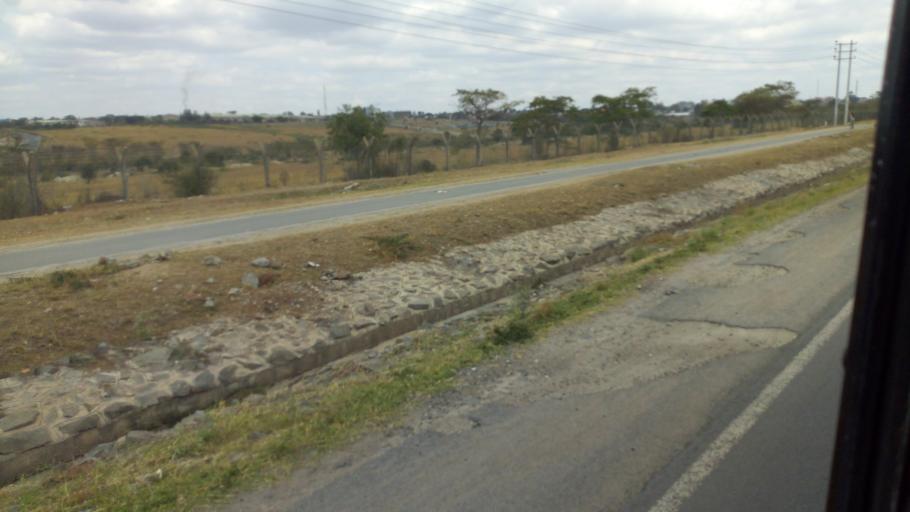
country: KE
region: Machakos
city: Athi River
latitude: -1.4615
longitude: 36.9638
